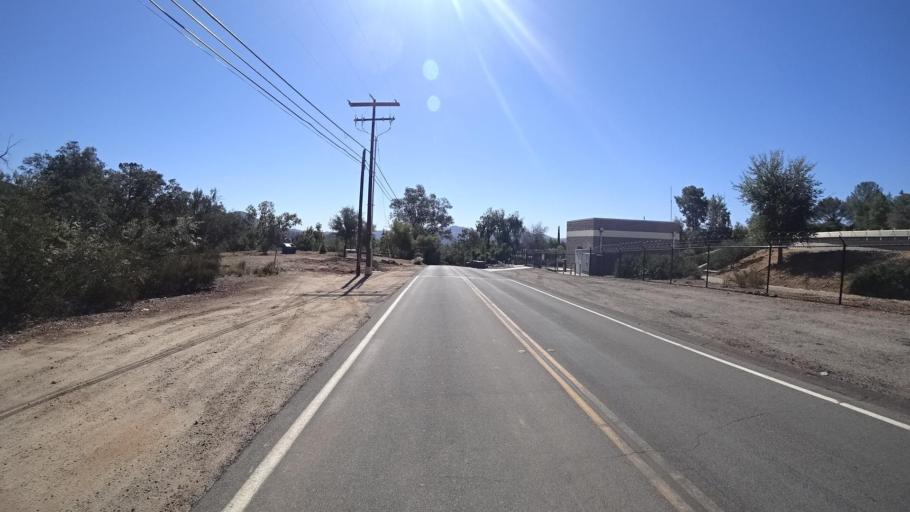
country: US
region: California
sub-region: San Diego County
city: Alpine
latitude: 32.8433
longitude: -116.7478
